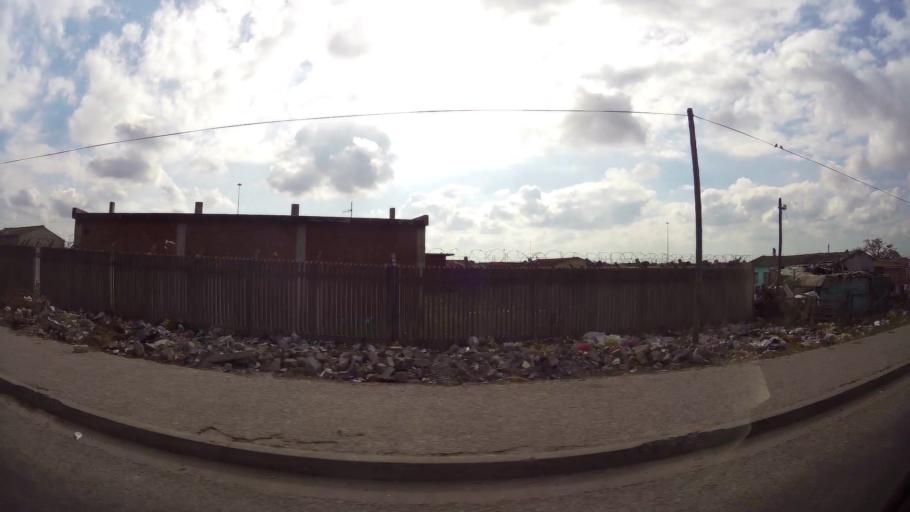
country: ZA
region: Eastern Cape
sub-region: Nelson Mandela Bay Metropolitan Municipality
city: Port Elizabeth
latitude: -33.8075
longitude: 25.5866
